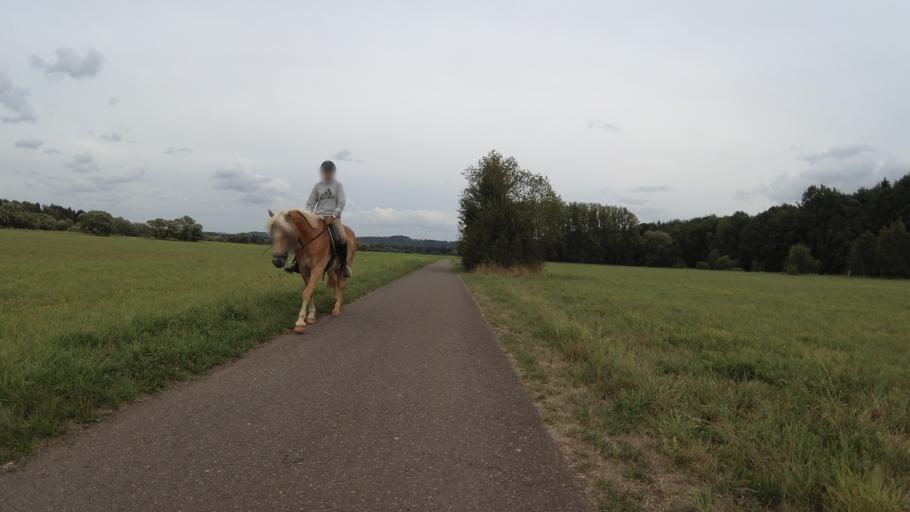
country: DE
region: Saarland
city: Bexbach
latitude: 49.3131
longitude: 7.2881
